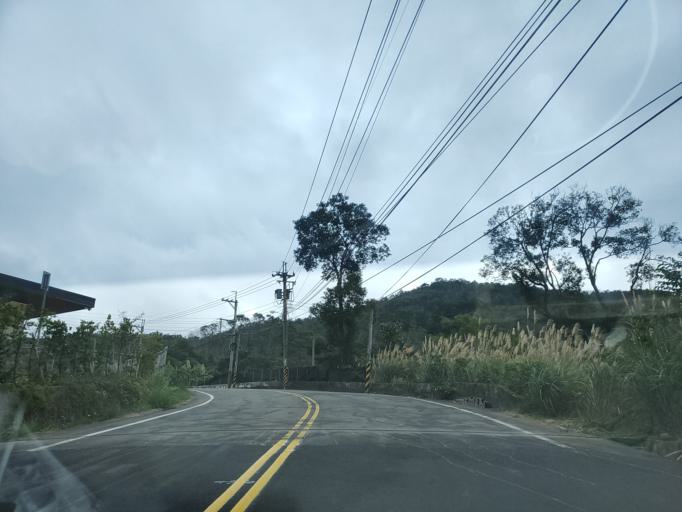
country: TW
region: Taiwan
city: Fengyuan
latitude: 24.3746
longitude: 120.7663
